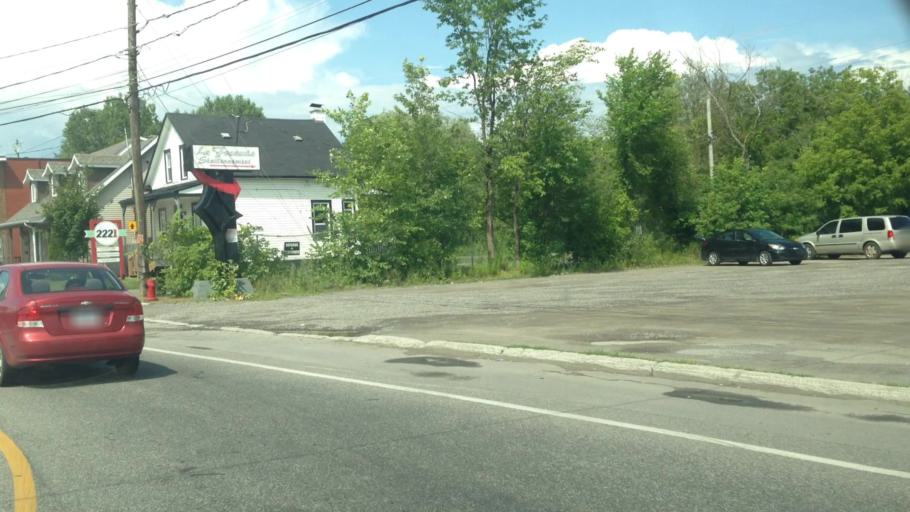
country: CA
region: Quebec
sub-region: Laurentides
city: Saint-Jerome
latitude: 45.8062
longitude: -74.0125
